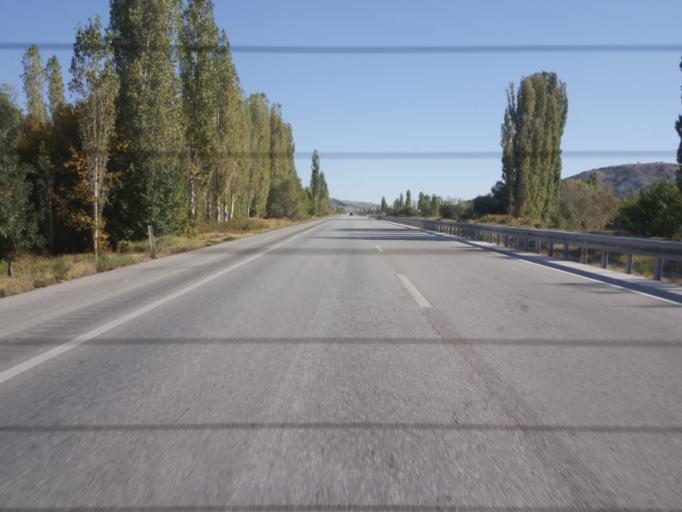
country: TR
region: Corum
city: Sungurlu
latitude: 40.1888
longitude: 34.4985
